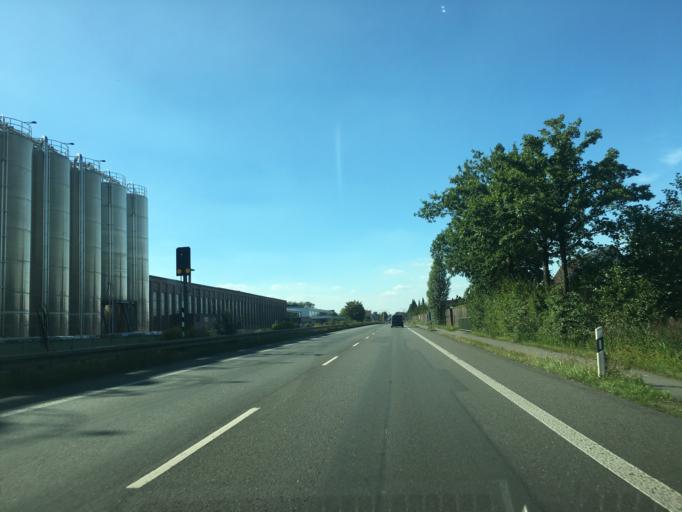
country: DE
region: North Rhine-Westphalia
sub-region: Regierungsbezirk Detmold
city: Rheda-Wiedenbruck
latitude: 51.8760
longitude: 8.2465
